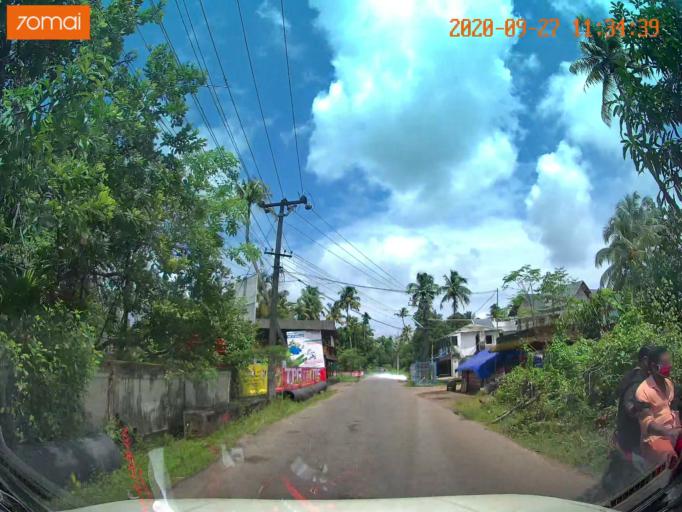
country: IN
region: Kerala
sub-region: Thrissur District
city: Thanniyam
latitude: 10.4381
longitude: 76.1262
